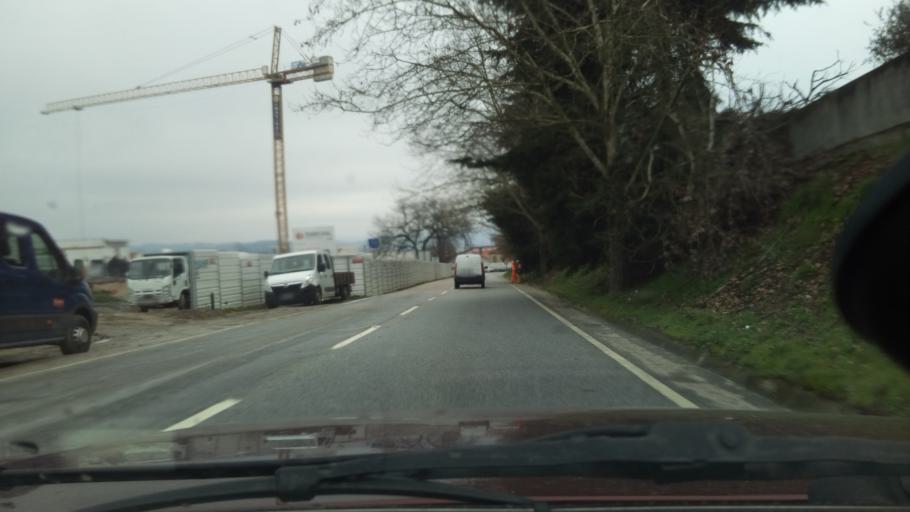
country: PT
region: Viseu
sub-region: Viseu
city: Rio de Loba
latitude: 40.6400
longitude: -7.8580
